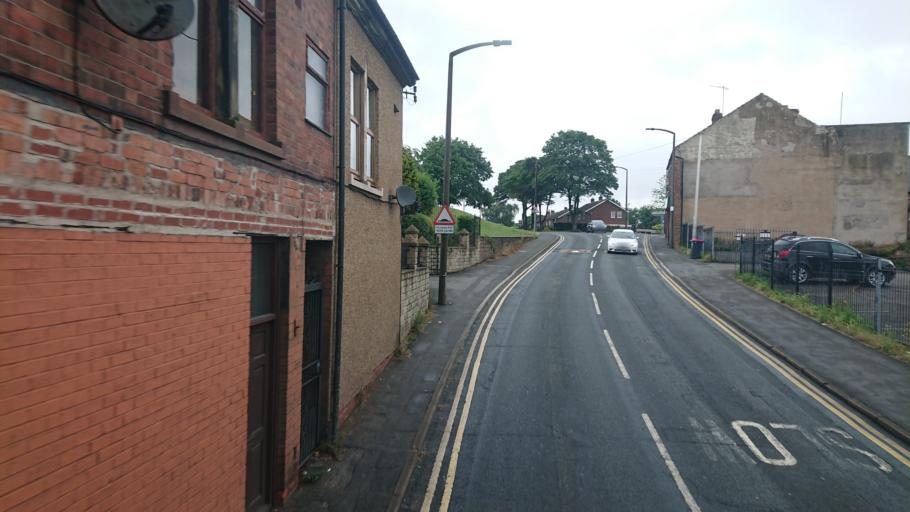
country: GB
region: England
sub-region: Rotherham
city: Catcliffe
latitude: 53.3921
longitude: -1.3616
